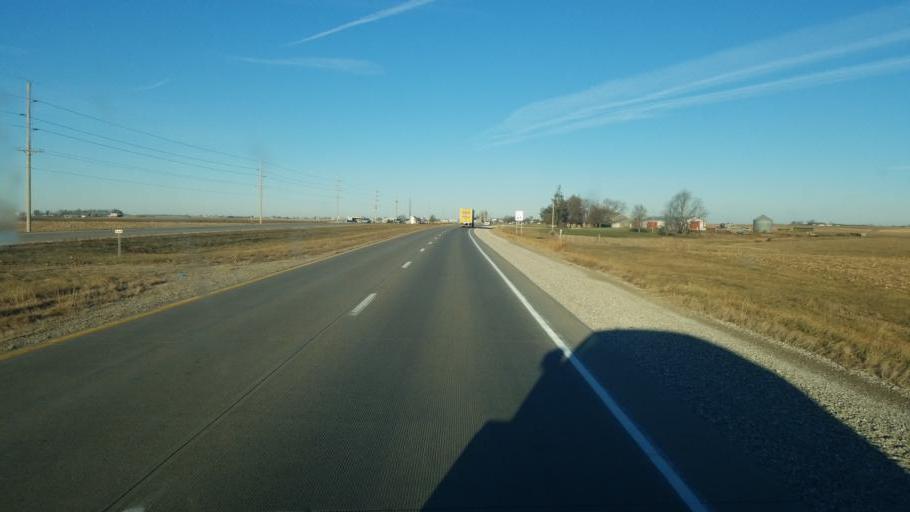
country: US
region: Iowa
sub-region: Marion County
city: Pella
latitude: 41.3649
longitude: -92.7876
